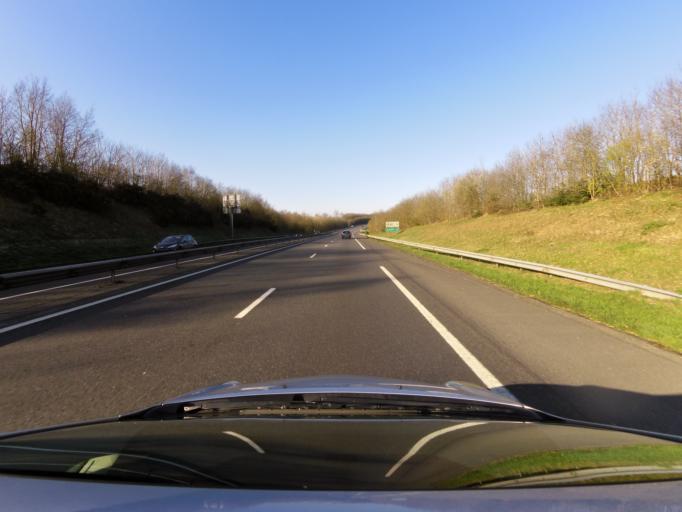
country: FR
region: Lower Normandy
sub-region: Departement du Calvados
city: Saint-Martin-des-Besaces
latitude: 49.0175
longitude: -0.8465
